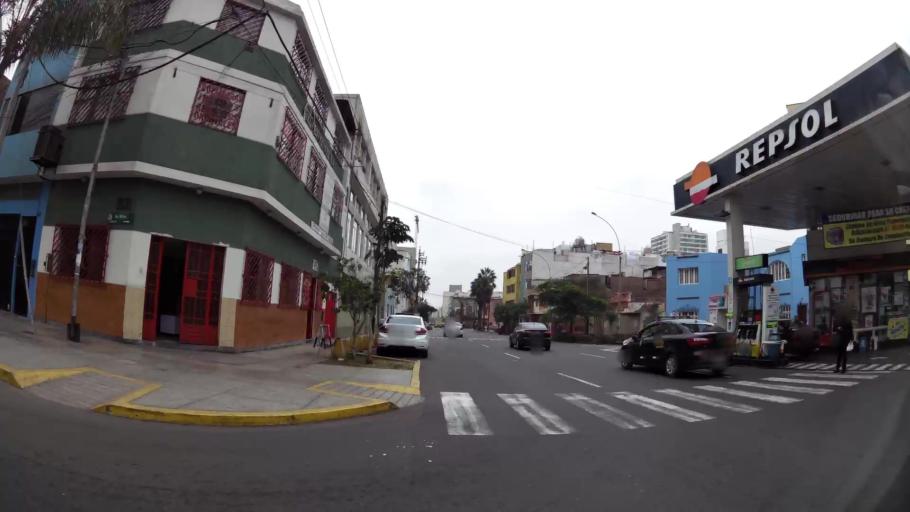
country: PE
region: Lima
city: Lima
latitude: -12.0803
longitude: -77.0319
